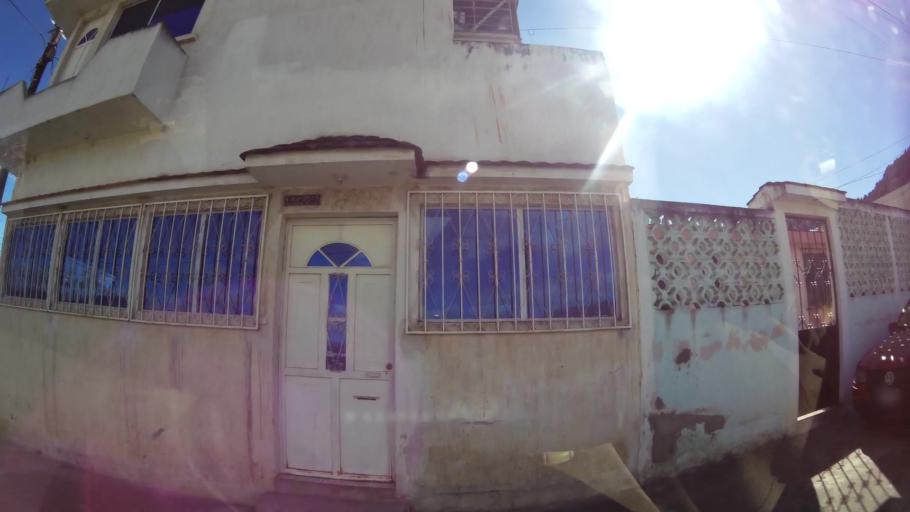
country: GT
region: Quetzaltenango
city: Quetzaltenango
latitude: 14.8379
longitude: -91.5045
